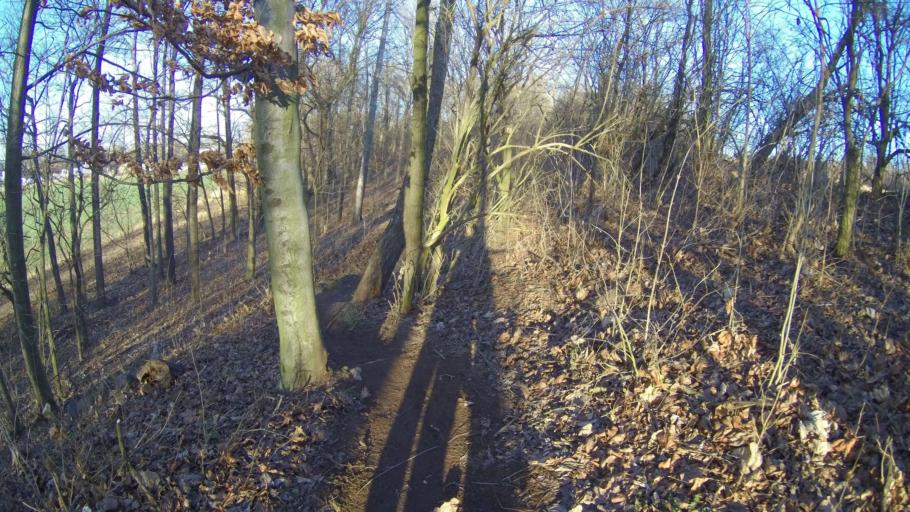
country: CZ
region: Central Bohemia
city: Neratovice
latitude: 50.2343
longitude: 14.5063
